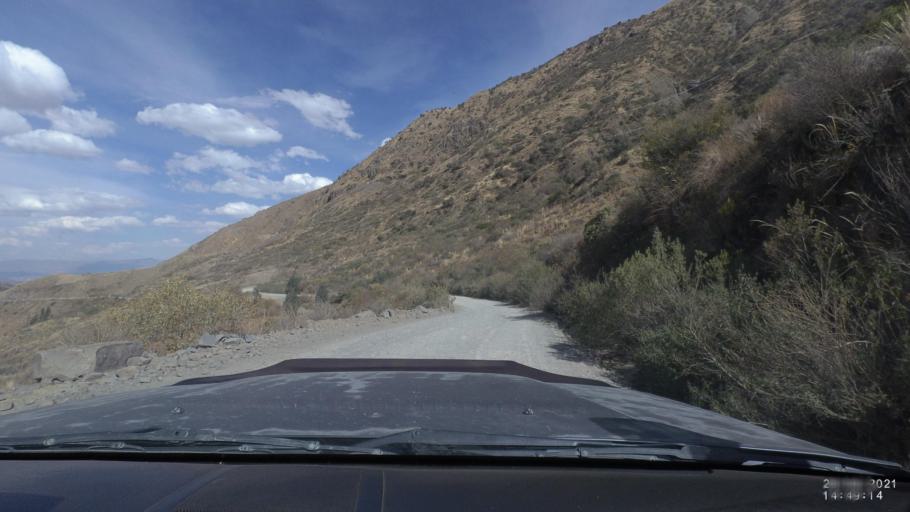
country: BO
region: Cochabamba
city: Sipe Sipe
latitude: -17.2818
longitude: -66.3166
